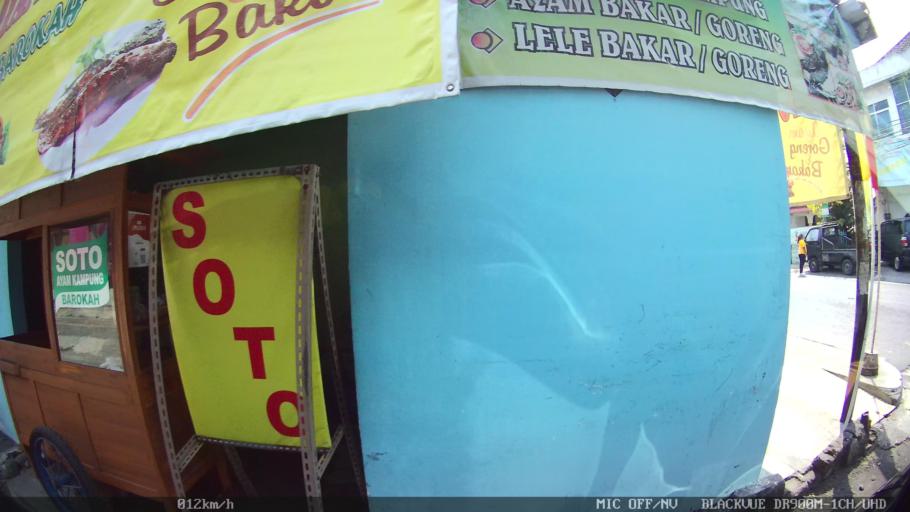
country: ID
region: Daerah Istimewa Yogyakarta
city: Yogyakarta
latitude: -7.8066
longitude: 110.3776
